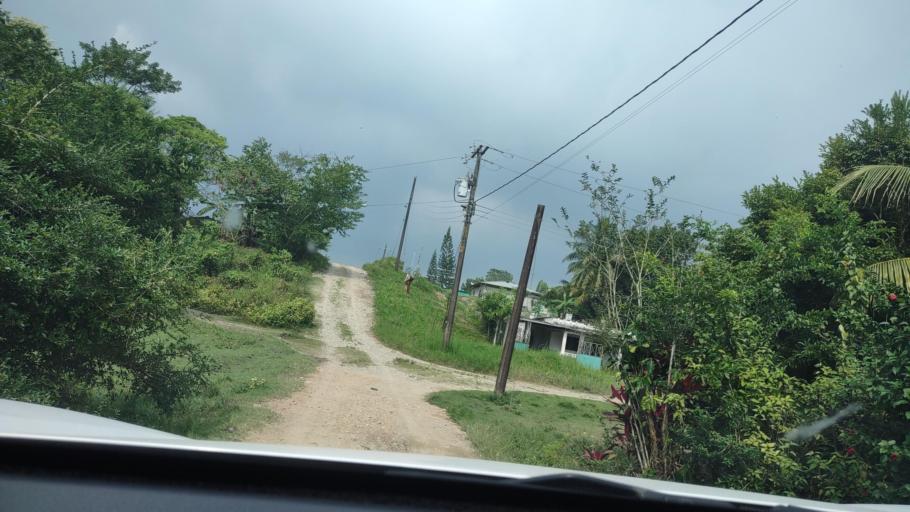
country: MX
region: Veracruz
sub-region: Uxpanapa
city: Poblado 10
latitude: 17.5461
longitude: -94.2936
